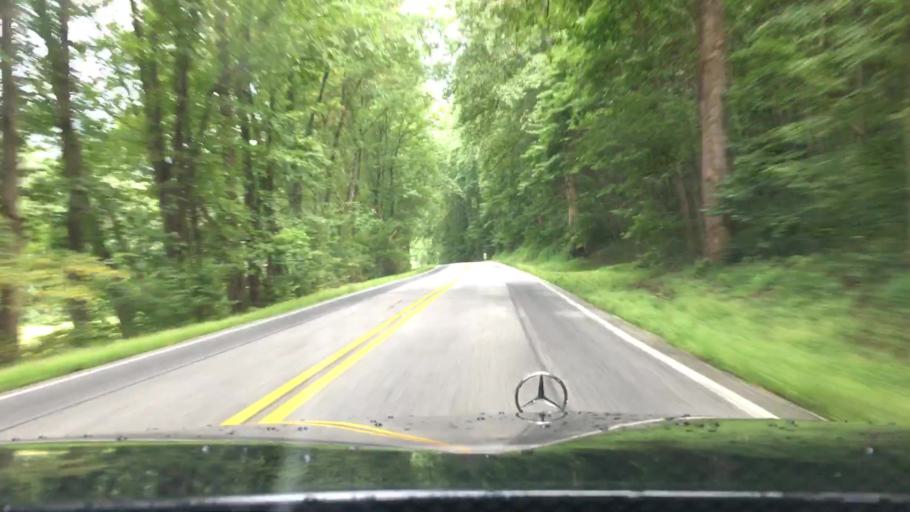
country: US
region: Virginia
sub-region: Nelson County
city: Nellysford
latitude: 37.8411
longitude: -78.9278
